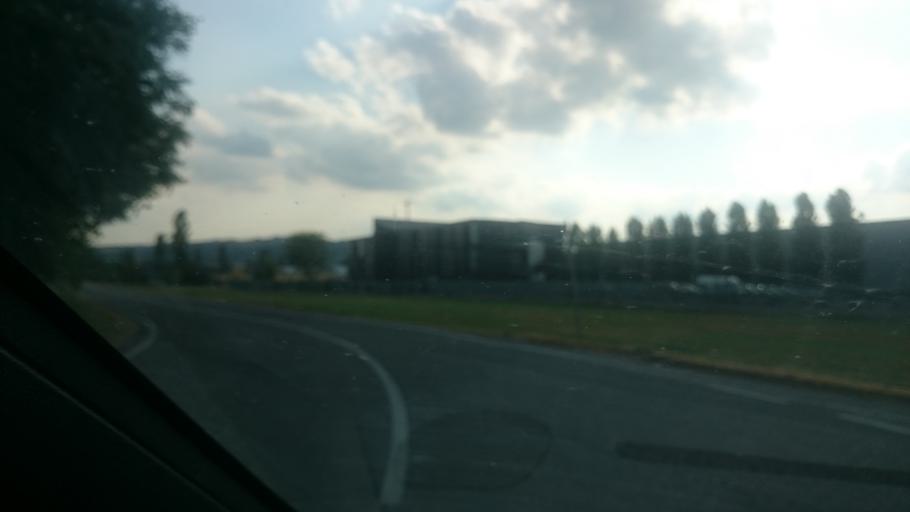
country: IT
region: Emilia-Romagna
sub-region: Provincia di Reggio Emilia
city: Salvaterra
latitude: 44.5896
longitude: 10.7651
